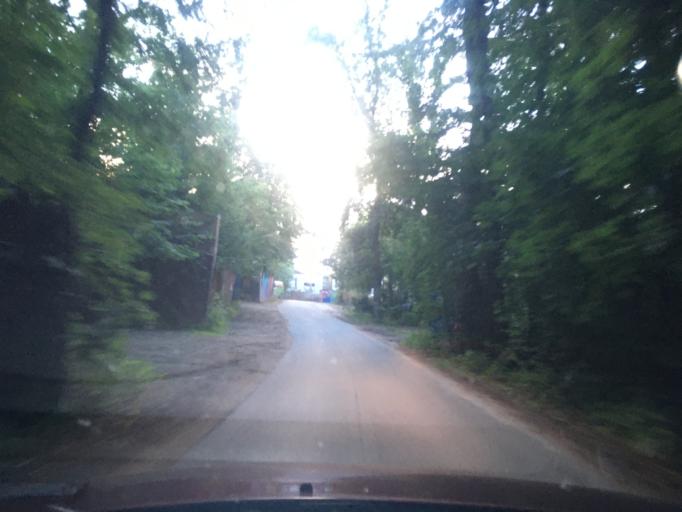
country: PL
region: Lower Silesian Voivodeship
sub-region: Powiat zgorzelecki
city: Piensk
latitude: 51.2937
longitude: 15.0232
